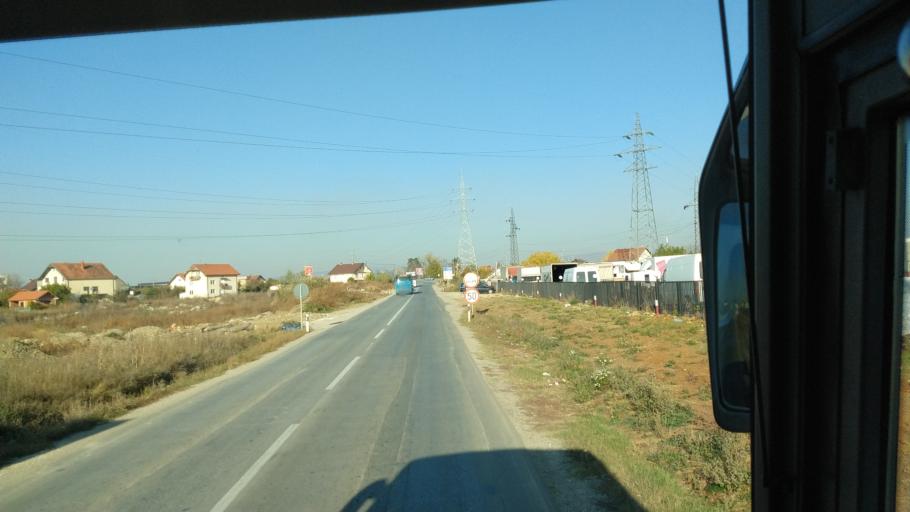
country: XK
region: Pristina
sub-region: Lipjan
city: Lipljan
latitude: 42.5309
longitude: 21.1146
